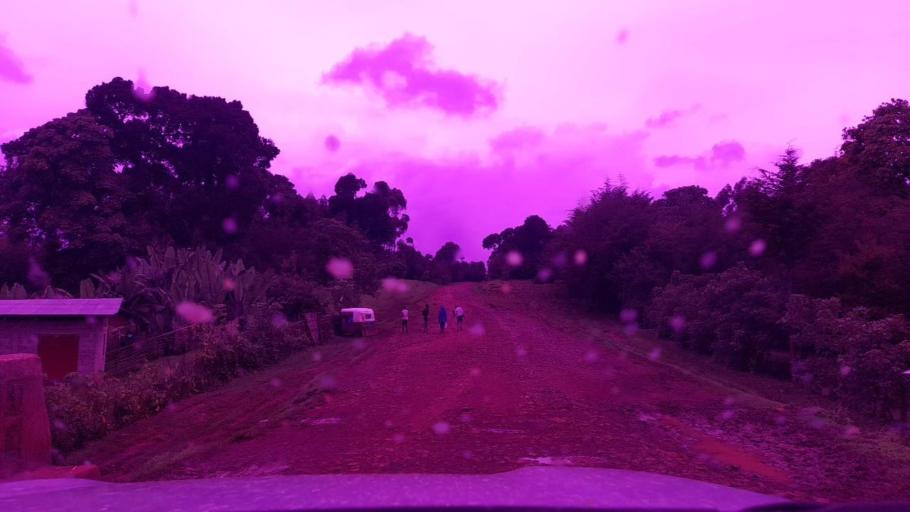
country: ET
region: Southern Nations, Nationalities, and People's Region
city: Tippi
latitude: 7.5747
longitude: 35.6645
